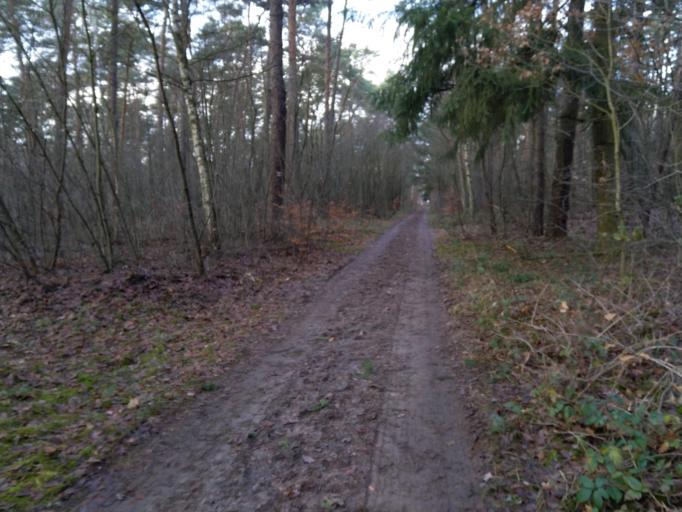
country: DE
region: Brandenburg
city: Bernau bei Berlin
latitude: 52.6331
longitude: 13.6367
